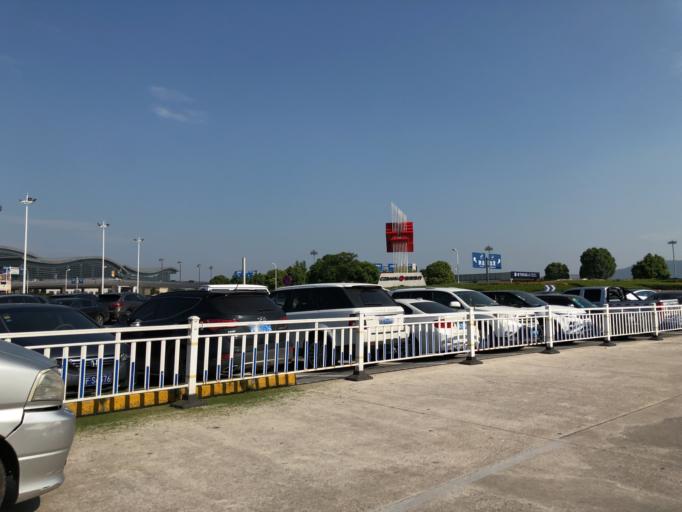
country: CN
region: Zhejiang Sheng
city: Nanyang
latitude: 30.2364
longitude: 120.4286
